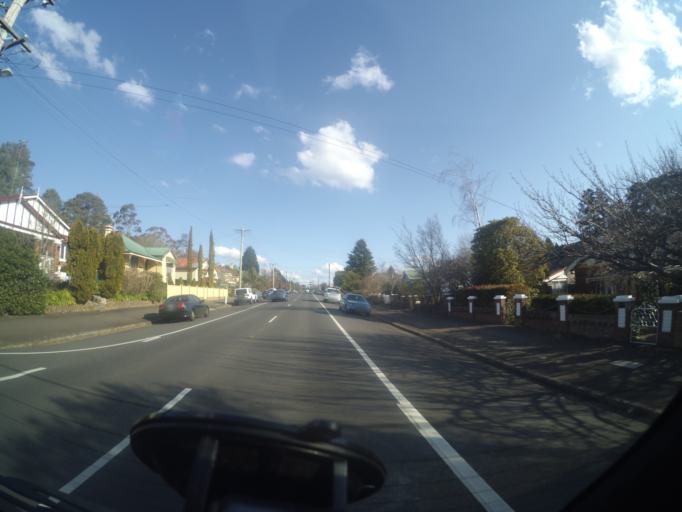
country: AU
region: New South Wales
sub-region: Blue Mountains Municipality
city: Katoomba
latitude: -33.7215
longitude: 150.3117
